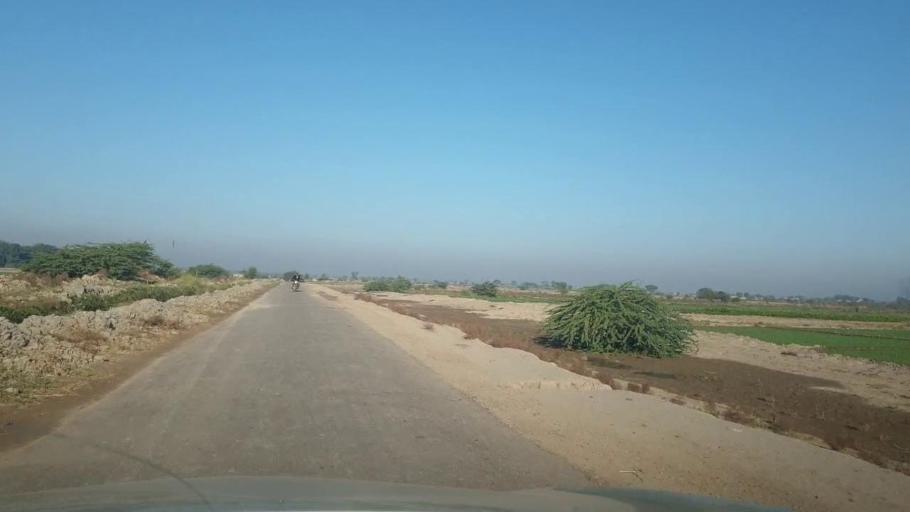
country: PK
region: Sindh
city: Bhan
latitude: 26.5515
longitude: 67.6977
